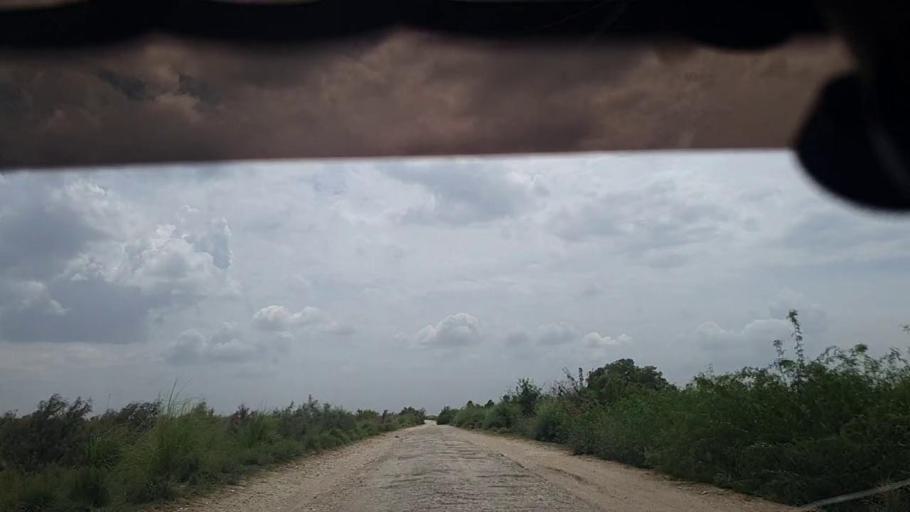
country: PK
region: Sindh
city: Rustam jo Goth
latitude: 28.0562
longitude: 68.9397
